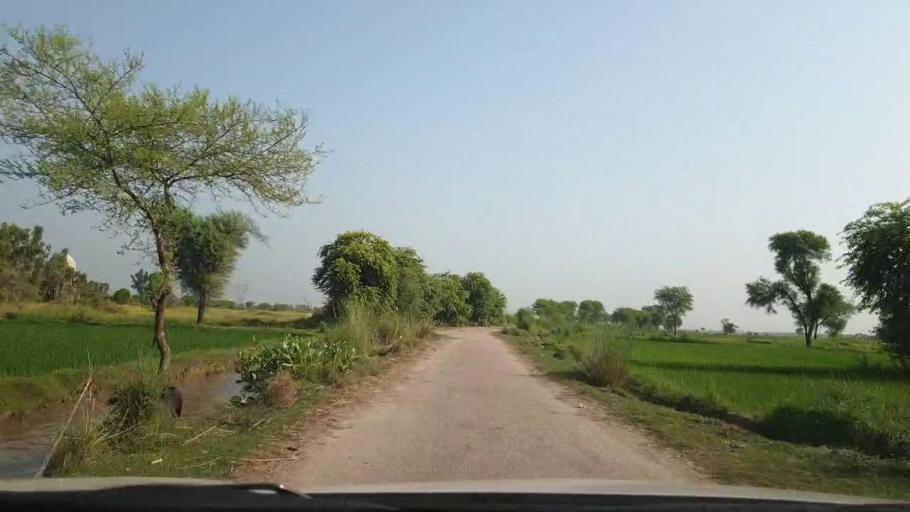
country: PK
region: Sindh
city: Goth Garelo
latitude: 27.4727
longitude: 68.1185
